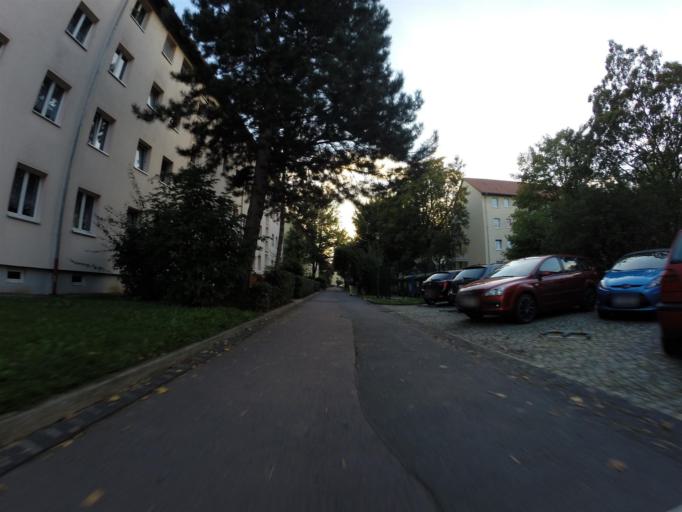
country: DE
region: Thuringia
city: Jena
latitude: 50.9438
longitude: 11.5983
